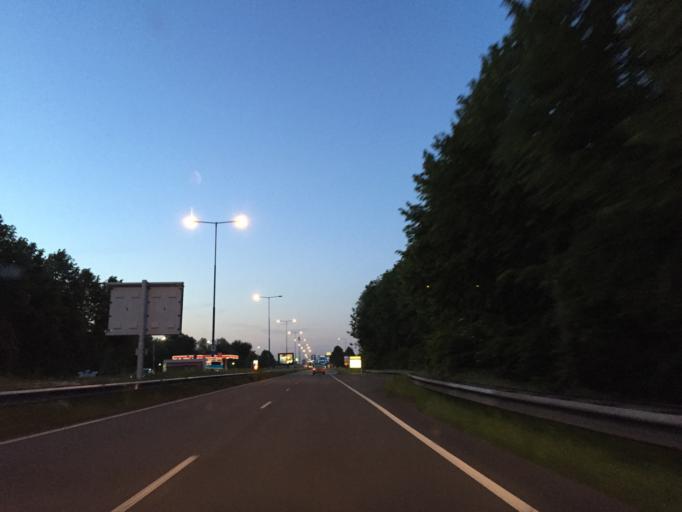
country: NL
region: South Holland
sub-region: Gemeente Zoetermeer
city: Zoetermeer
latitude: 52.0492
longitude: 4.5146
